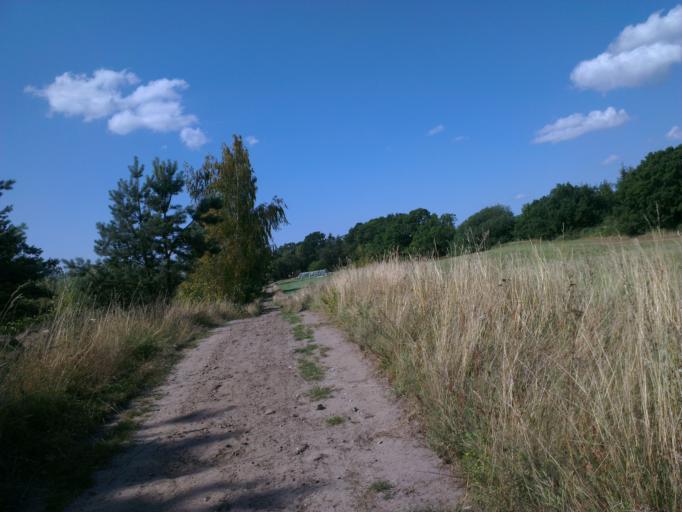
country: DK
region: Capital Region
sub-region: Frederikssund Kommune
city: Frederikssund
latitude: 55.8810
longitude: 12.0752
